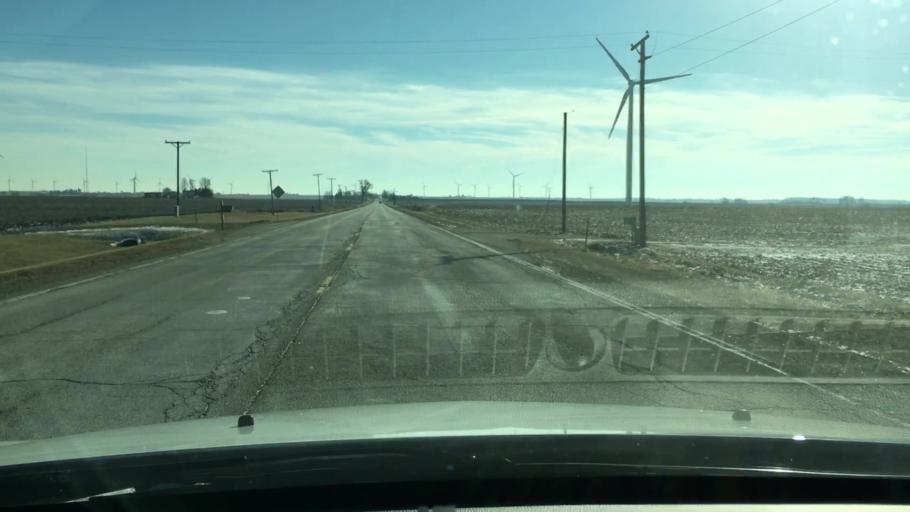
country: US
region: Illinois
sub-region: LaSalle County
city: Mendota
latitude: 41.6802
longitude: -89.1298
